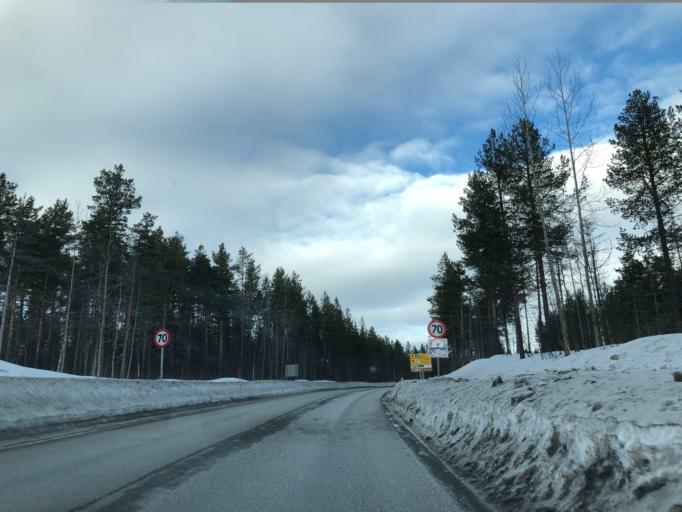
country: NO
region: Troms
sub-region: Malselv
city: Moen
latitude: 69.1298
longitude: 18.5759
